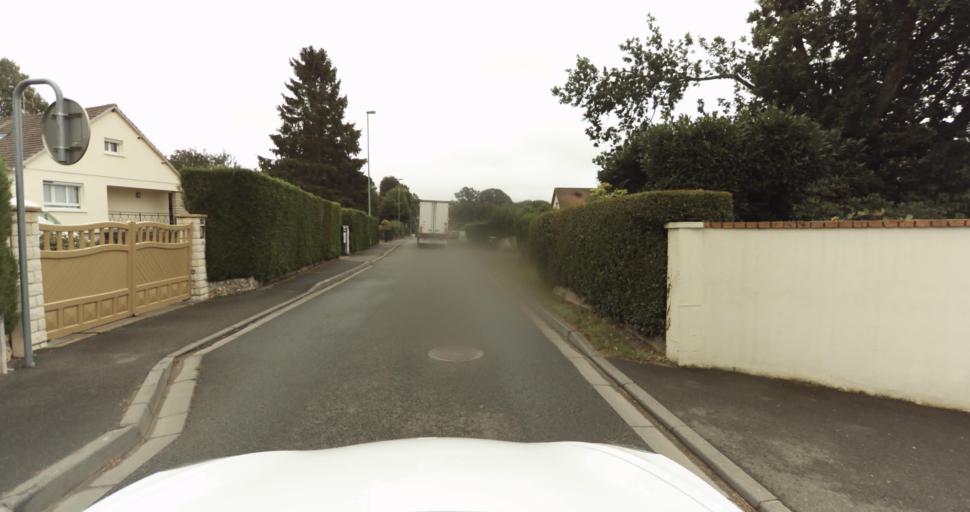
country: FR
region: Haute-Normandie
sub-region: Departement de l'Eure
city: Aviron
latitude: 49.0505
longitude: 1.1258
